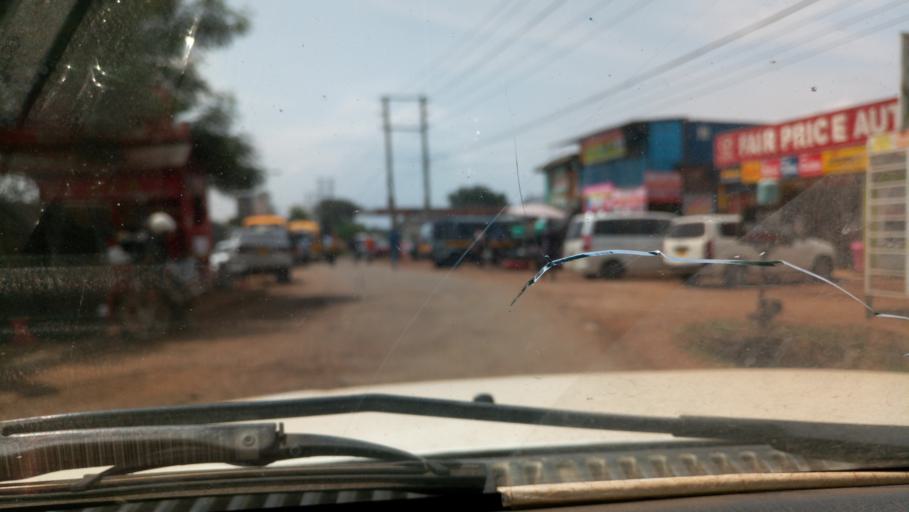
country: KE
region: Kiambu
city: Kikuyu
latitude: -1.2649
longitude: 36.7373
